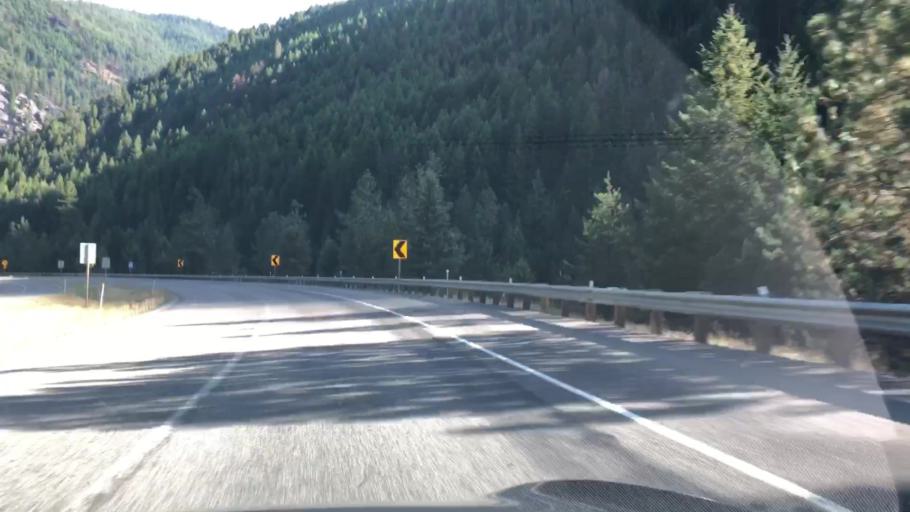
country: US
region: Montana
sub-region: Sanders County
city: Thompson Falls
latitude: 47.3176
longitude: -115.2438
